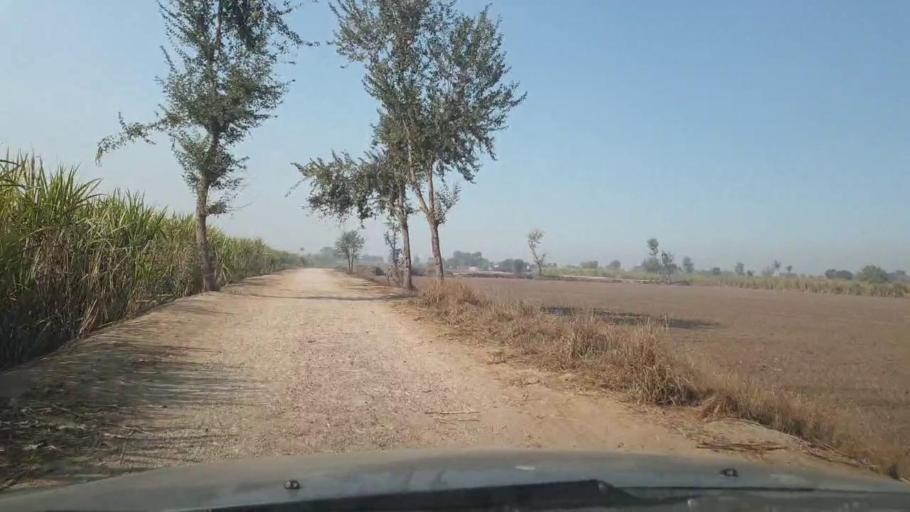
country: PK
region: Sindh
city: Ghotki
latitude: 28.0284
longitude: 69.2513
